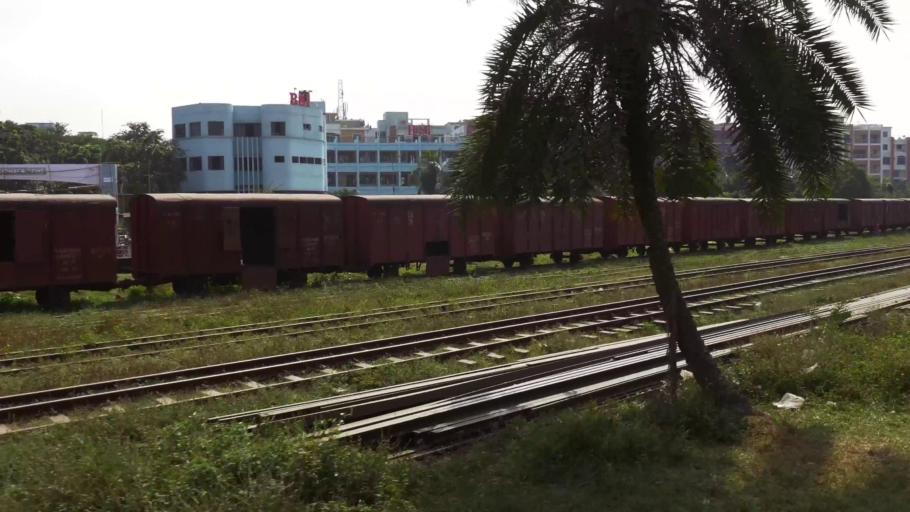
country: BD
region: Dhaka
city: Tungi
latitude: 23.8688
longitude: 90.4061
